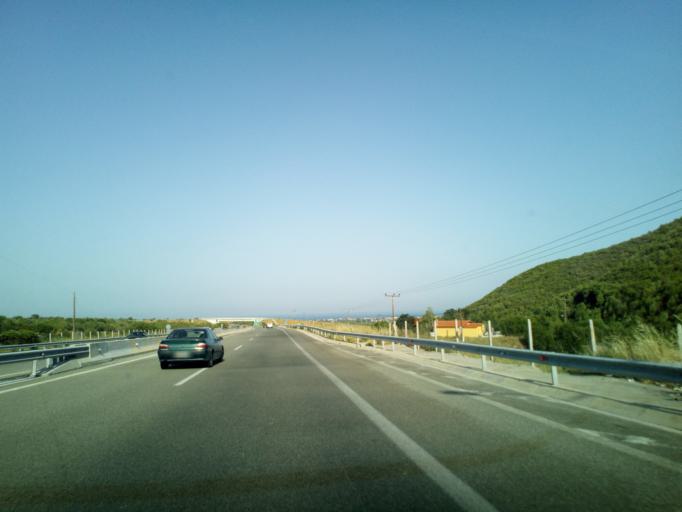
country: GR
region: Central Macedonia
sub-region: Nomos Thessalonikis
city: Nea Vrasna
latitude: 40.7010
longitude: 23.6539
